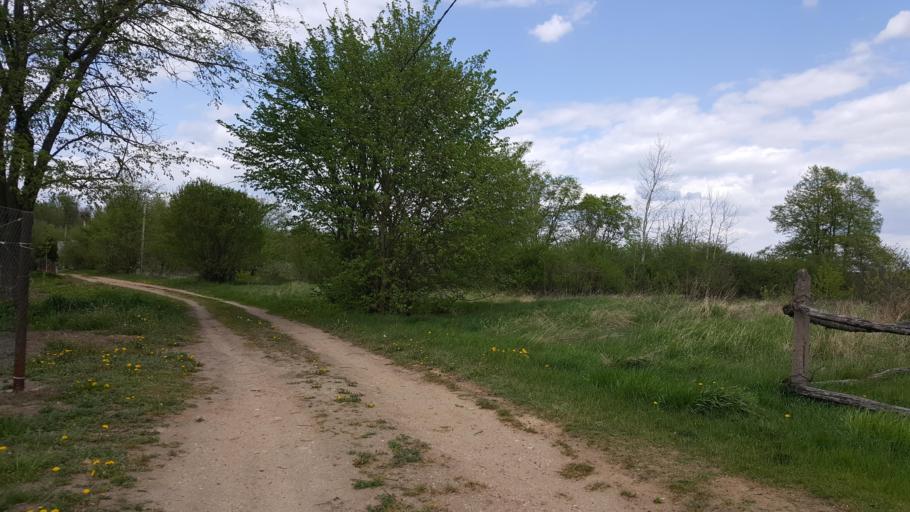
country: BY
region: Brest
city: Zhabinka
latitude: 52.3952
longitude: 24.0958
